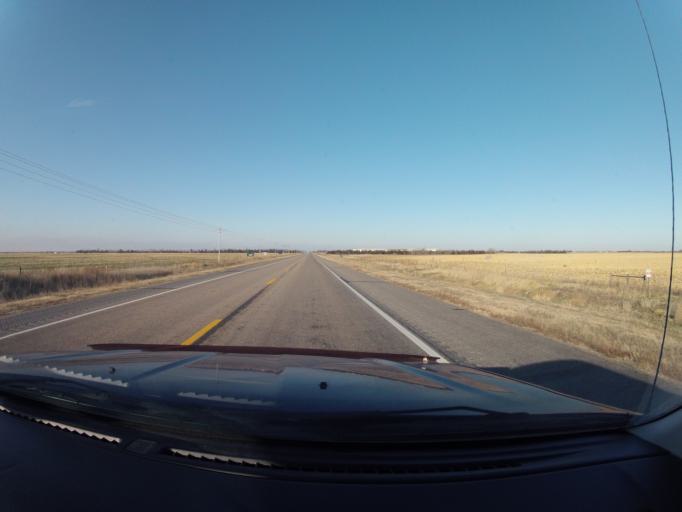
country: US
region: Nebraska
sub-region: Kearney County
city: Minden
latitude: 40.6228
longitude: -98.9515
